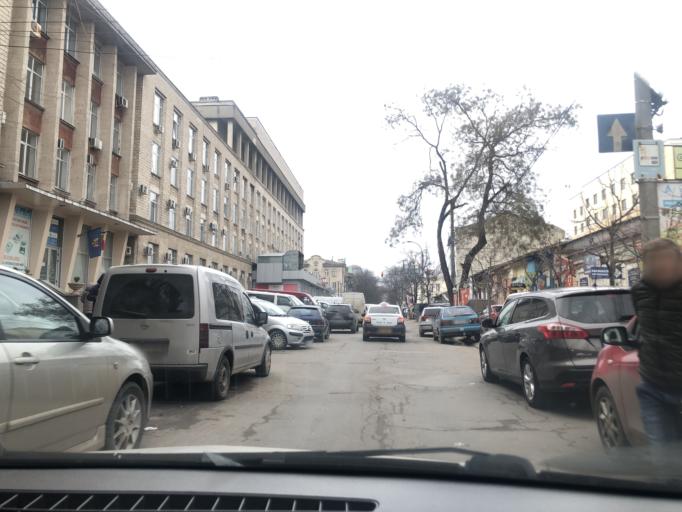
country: MD
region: Chisinau
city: Chisinau
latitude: 47.0215
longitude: 28.8413
